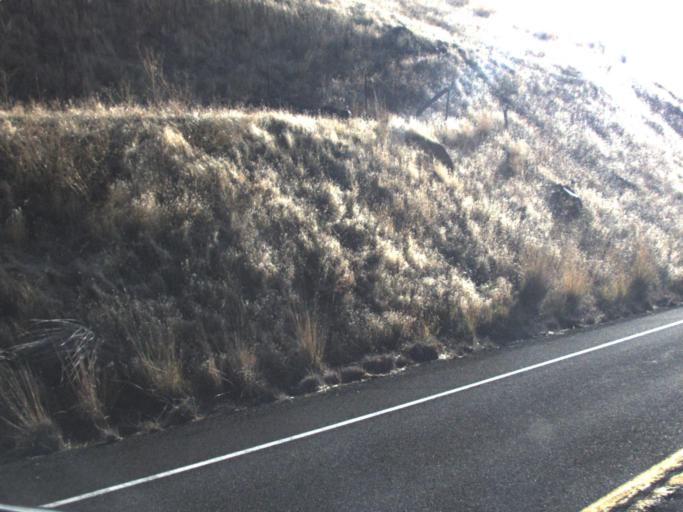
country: US
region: Washington
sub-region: Garfield County
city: Pomeroy
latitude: 46.4523
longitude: -117.4707
